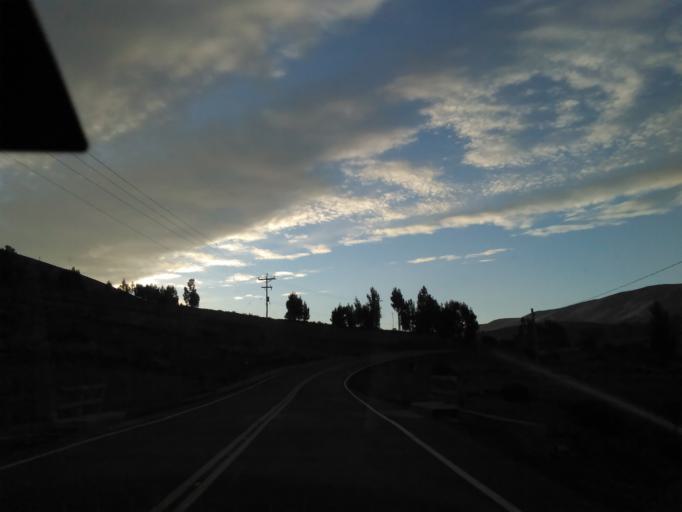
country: BO
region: Cochabamba
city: Arani
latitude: -17.6150
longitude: -65.6644
